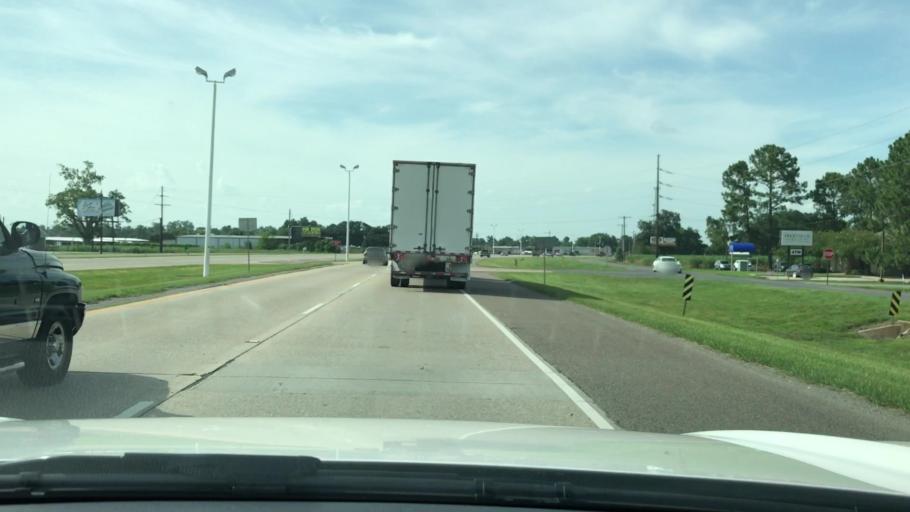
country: US
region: Louisiana
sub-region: West Baton Rouge Parish
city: Addis
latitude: 30.3597
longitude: -91.2605
